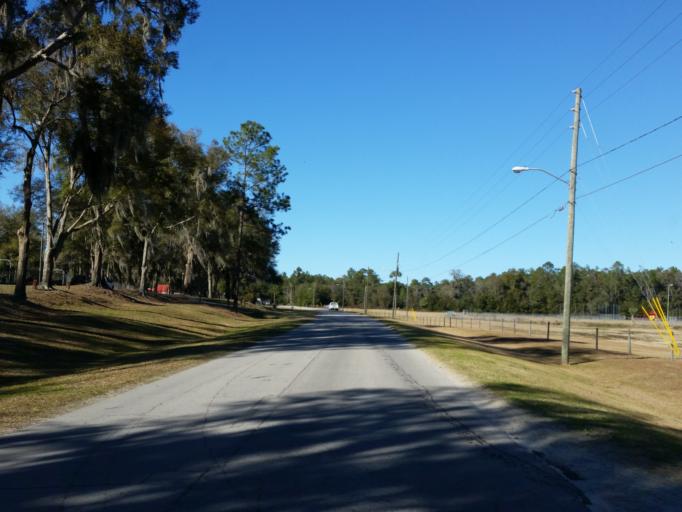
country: US
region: Florida
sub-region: Hamilton County
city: Jasper
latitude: 30.5064
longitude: -82.9528
